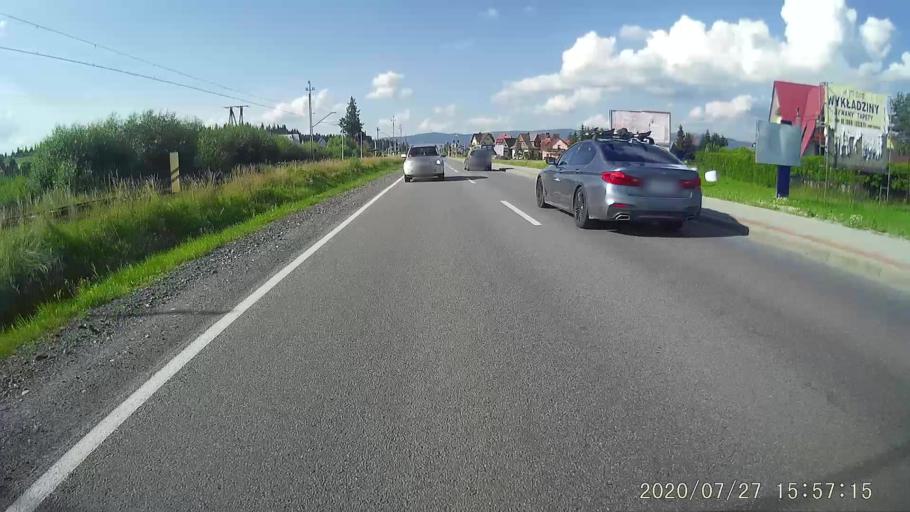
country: PL
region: Lesser Poland Voivodeship
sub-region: Powiat nowotarski
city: Szaflary
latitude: 49.4216
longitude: 20.0191
